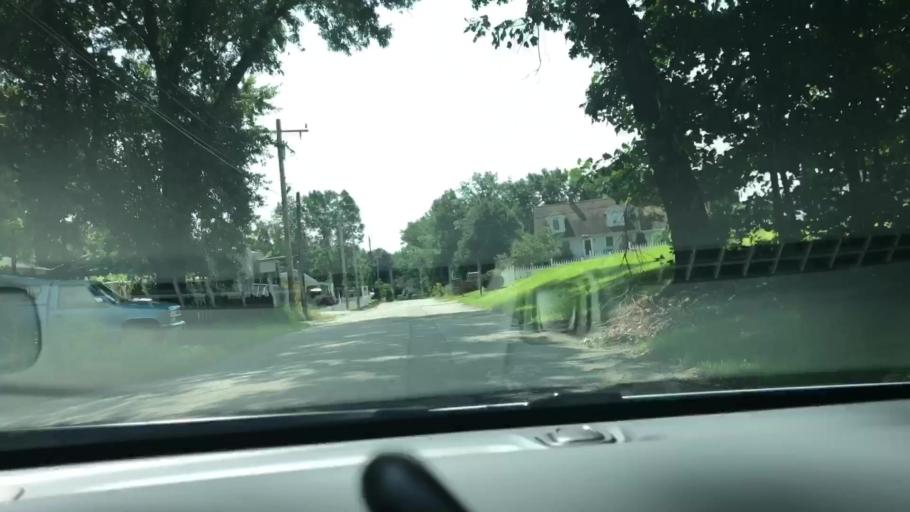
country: US
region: New Hampshire
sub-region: Hillsborough County
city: Pinardville
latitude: 42.9914
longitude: -71.5133
